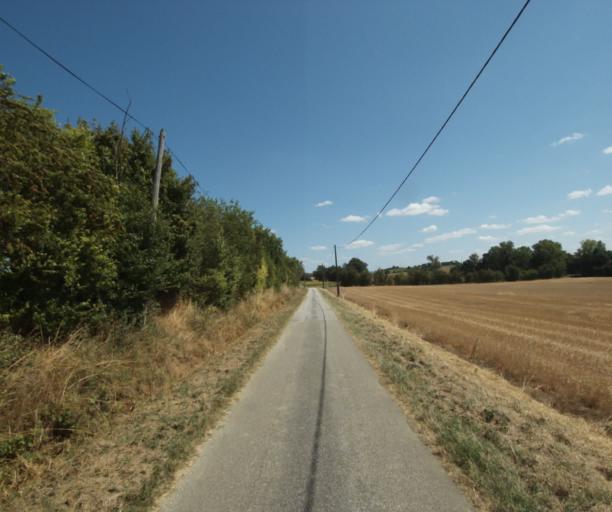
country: FR
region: Midi-Pyrenees
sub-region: Departement de la Haute-Garonne
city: Saint-Felix-Lauragais
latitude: 43.4854
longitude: 1.8974
